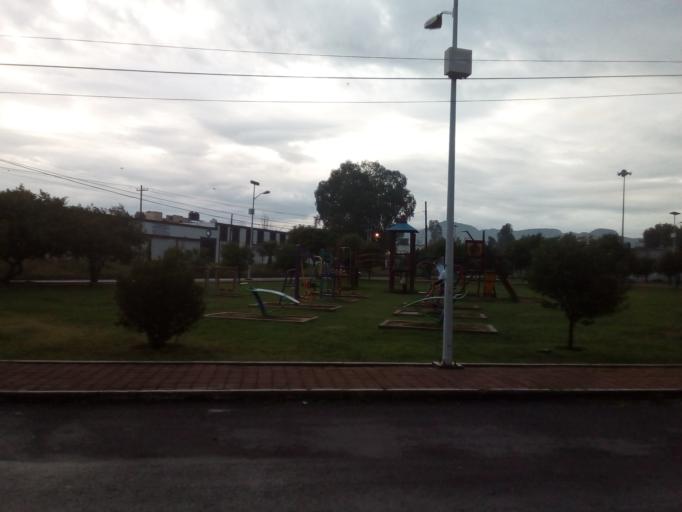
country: MX
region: Guanajuato
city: San Jose Iturbide
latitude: 21.0097
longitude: -100.3881
